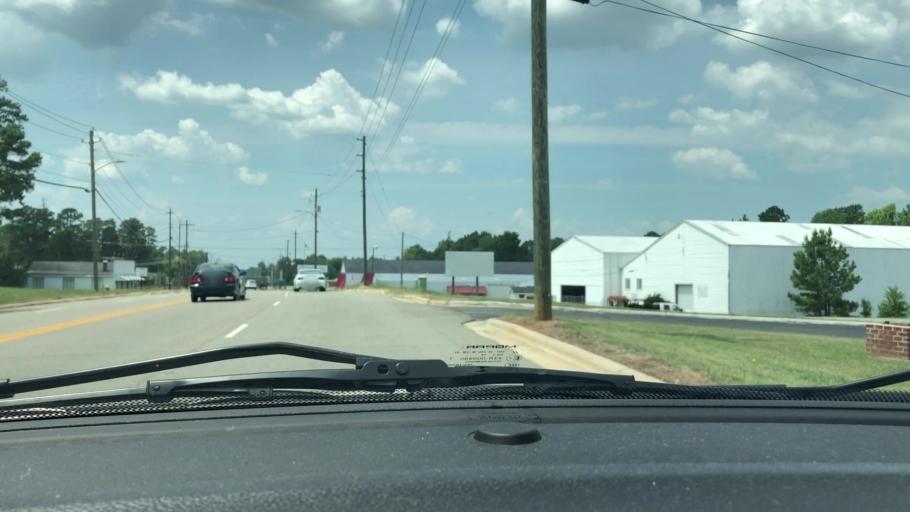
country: US
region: North Carolina
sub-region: Lee County
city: Sanford
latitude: 35.4919
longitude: -79.1907
